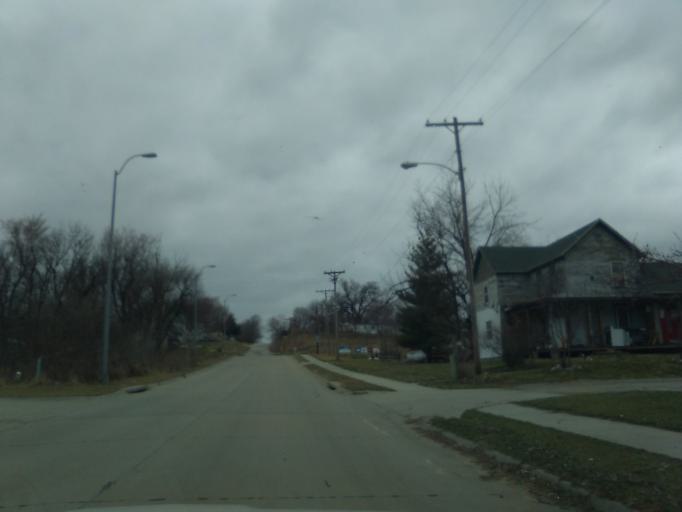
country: US
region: Nebraska
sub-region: Richardson County
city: Falls City
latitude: 40.0504
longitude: -95.4255
